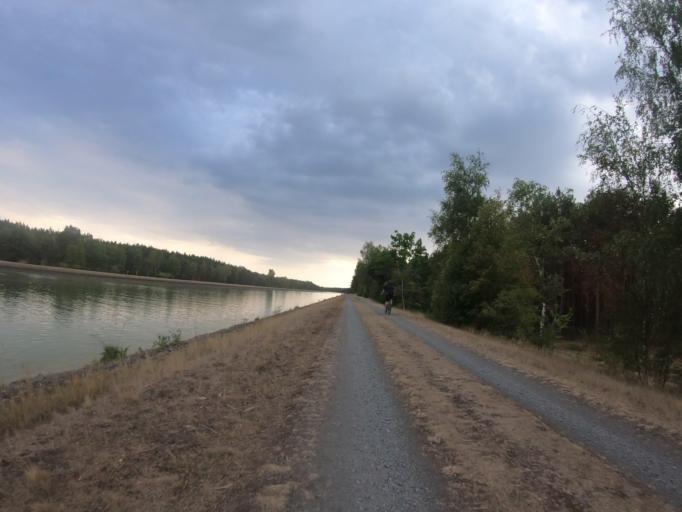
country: DE
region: Lower Saxony
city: Sassenburg
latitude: 52.5440
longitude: 10.6583
